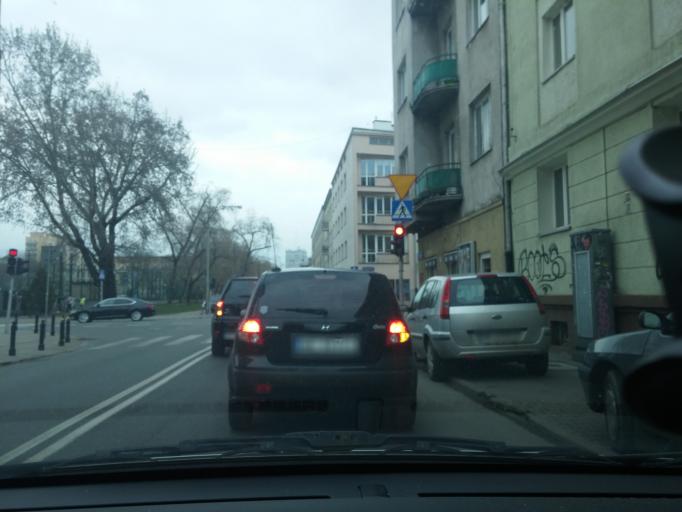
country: PL
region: Masovian Voivodeship
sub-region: Warszawa
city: Mokotow
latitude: 52.2039
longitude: 21.0146
